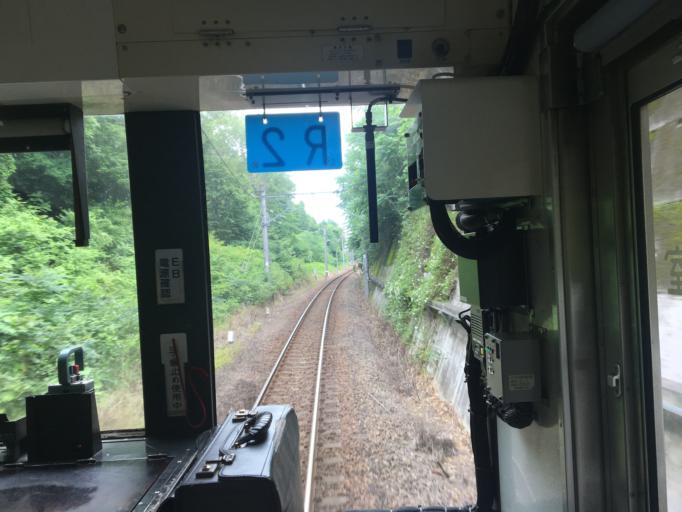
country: JP
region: Kanagawa
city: Zama
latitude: 35.5593
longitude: 139.3618
